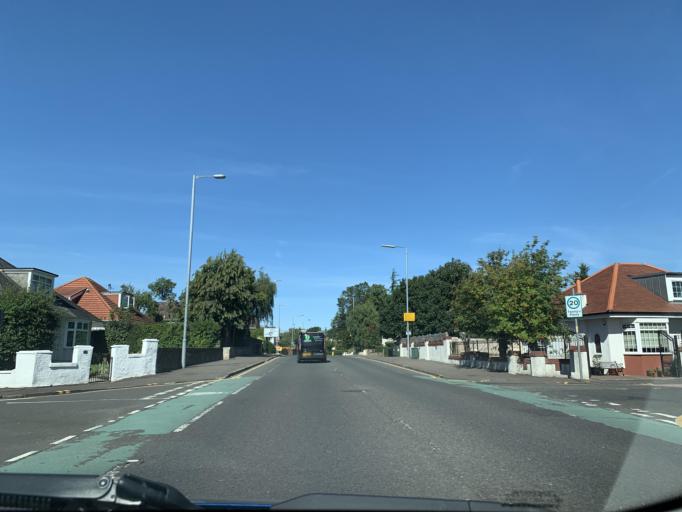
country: GB
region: Scotland
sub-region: East Renfrewshire
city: Giffnock
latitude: 55.8109
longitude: -4.2775
